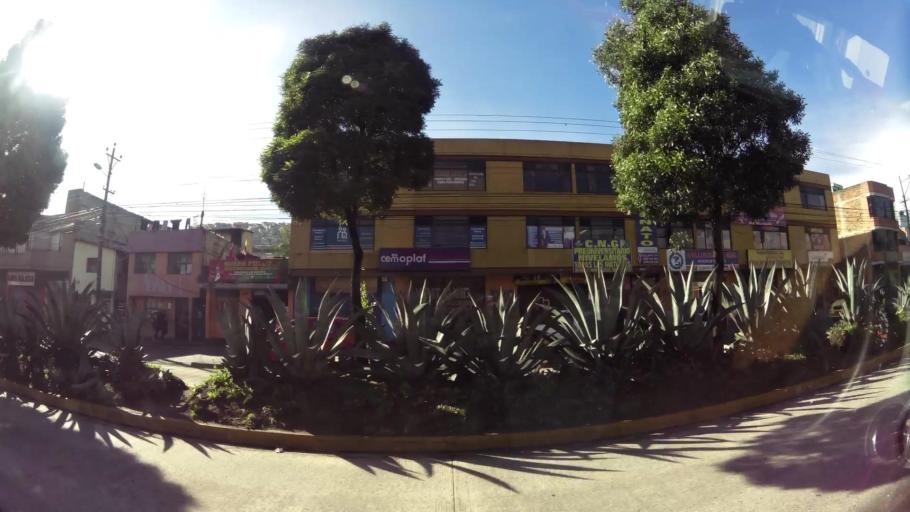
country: EC
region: Pichincha
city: Quito
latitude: -0.2847
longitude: -78.5363
